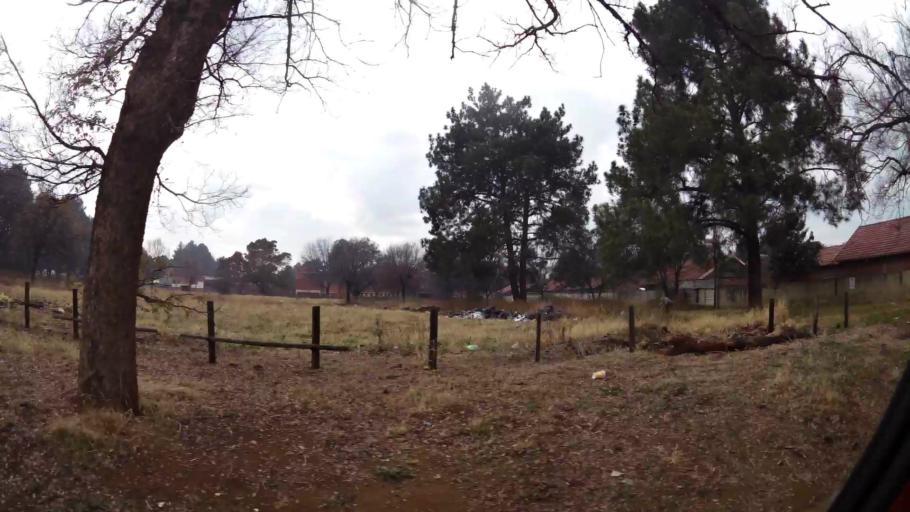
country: ZA
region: Gauteng
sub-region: Sedibeng District Municipality
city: Vanderbijlpark
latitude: -26.7009
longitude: 27.8422
